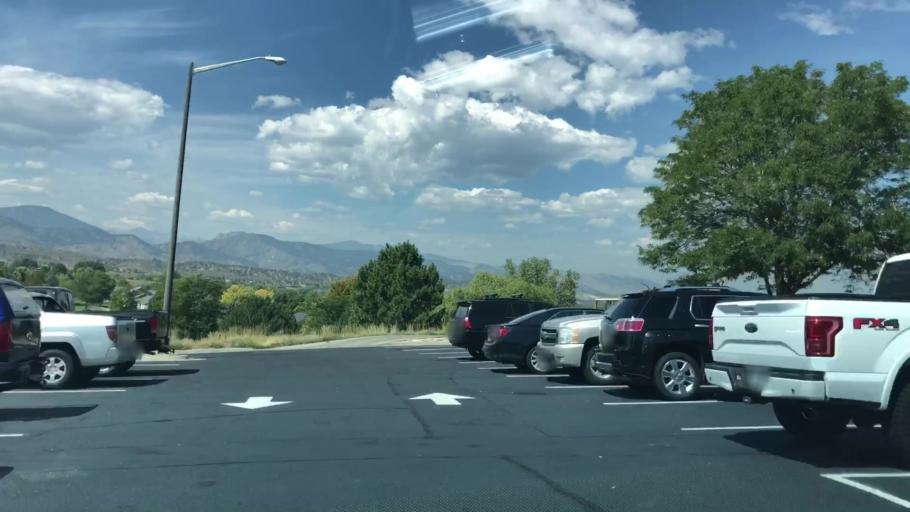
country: US
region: Colorado
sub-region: Larimer County
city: Loveland
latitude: 40.3985
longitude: -105.1426
